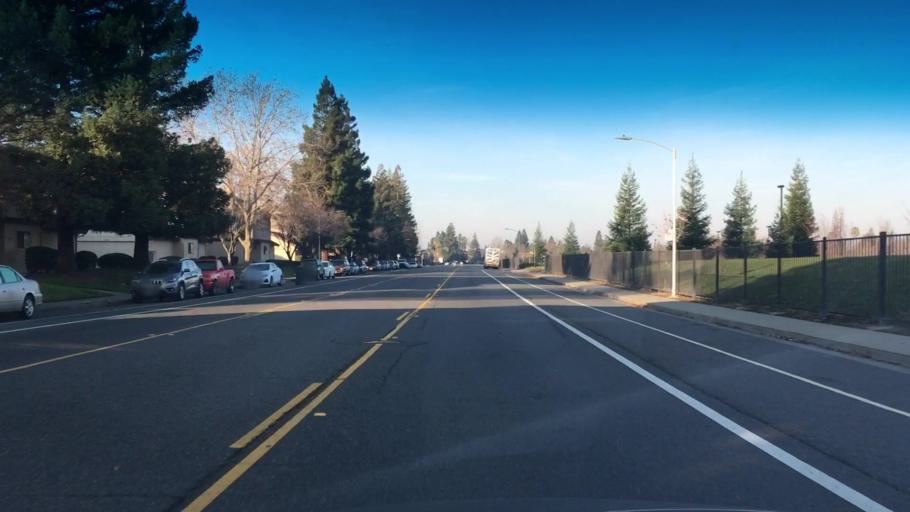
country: US
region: California
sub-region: Sacramento County
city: Laguna
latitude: 38.4498
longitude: -121.4220
